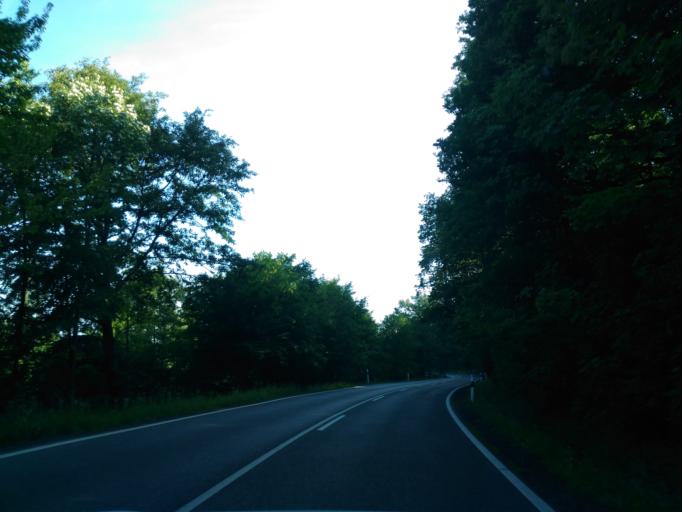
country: HU
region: Baranya
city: Komlo
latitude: 46.1806
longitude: 18.2621
